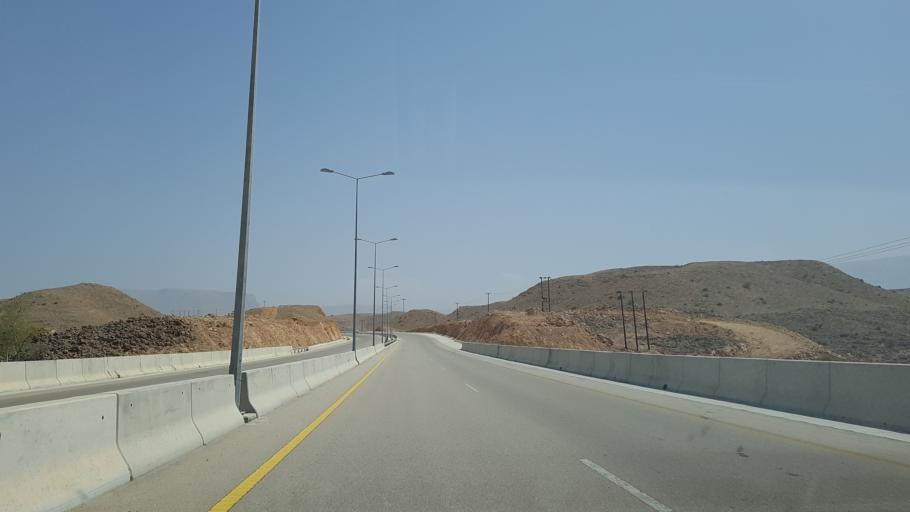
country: OM
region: Muhafazat Masqat
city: Muscat
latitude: 23.1344
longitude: 58.9720
